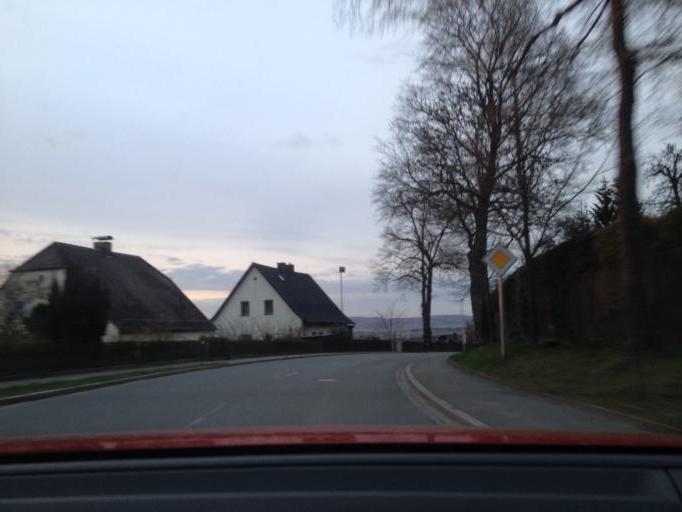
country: DE
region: Bavaria
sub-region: Upper Palatinate
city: Speinshart
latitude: 49.8275
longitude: 11.8387
